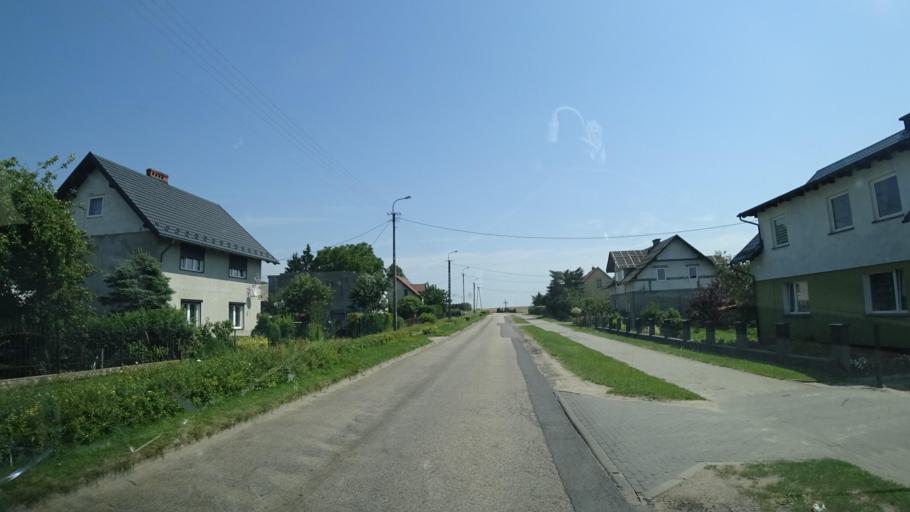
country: PL
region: Pomeranian Voivodeship
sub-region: Powiat chojnicki
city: Brusy
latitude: 53.8820
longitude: 17.6398
